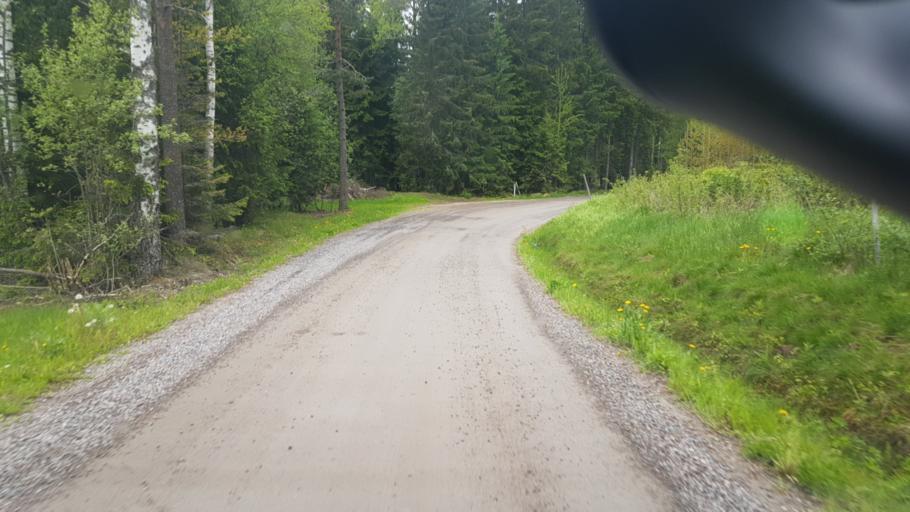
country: SE
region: Vaermland
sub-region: Eda Kommun
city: Charlottenberg
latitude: 59.8527
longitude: 12.3420
